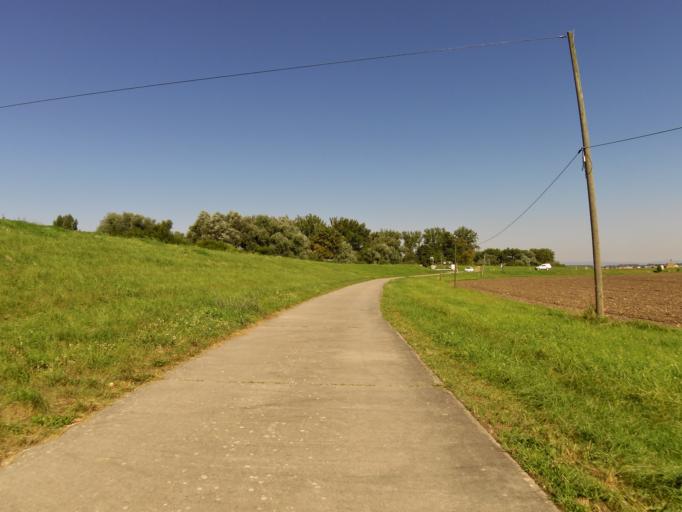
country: DE
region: Rheinland-Pfalz
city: Oppenheim
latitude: 49.8676
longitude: 8.3702
